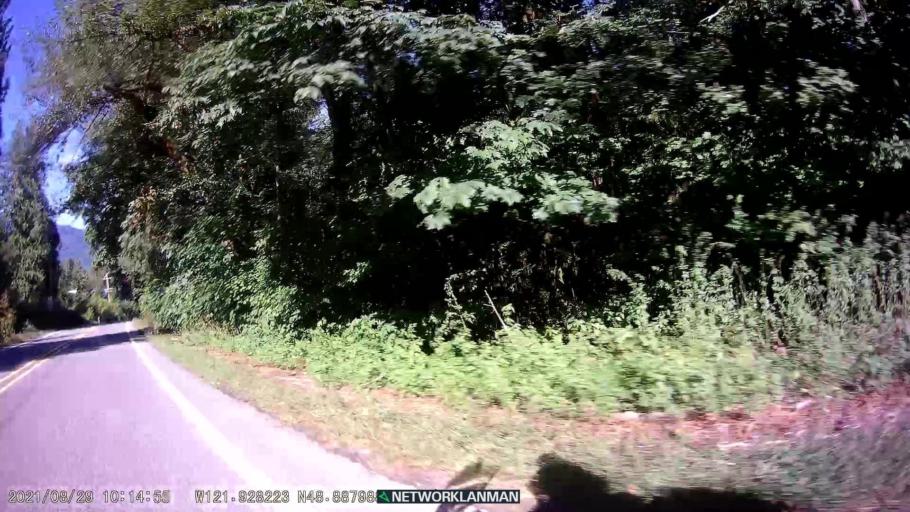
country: US
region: Washington
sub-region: Whatcom County
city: Peaceful Valley
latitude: 48.8880
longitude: -121.9286
